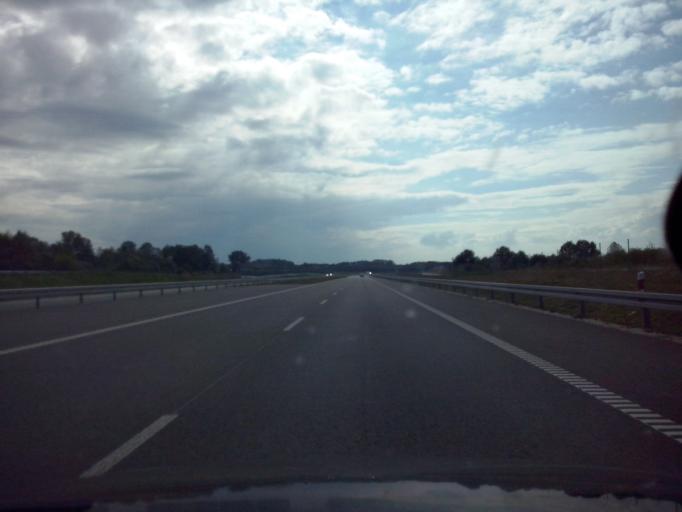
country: PL
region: Lesser Poland Voivodeship
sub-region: Powiat tarnowski
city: Lisia Gora
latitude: 50.0588
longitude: 21.0370
